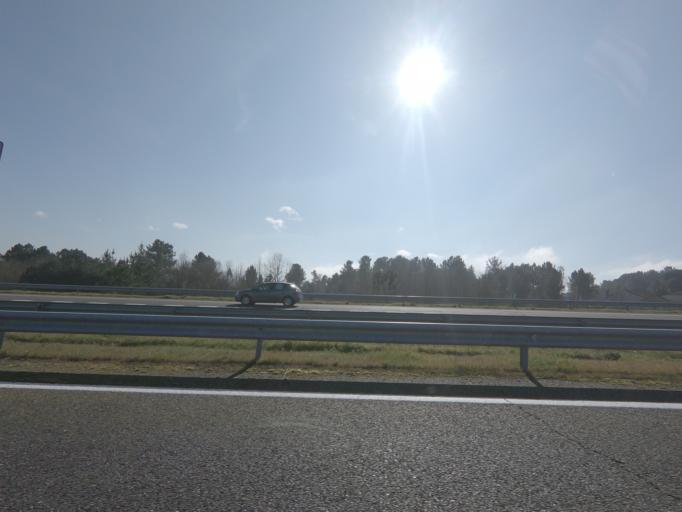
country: ES
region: Galicia
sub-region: Provincia de Ourense
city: Allariz
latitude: 42.2073
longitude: -7.8251
